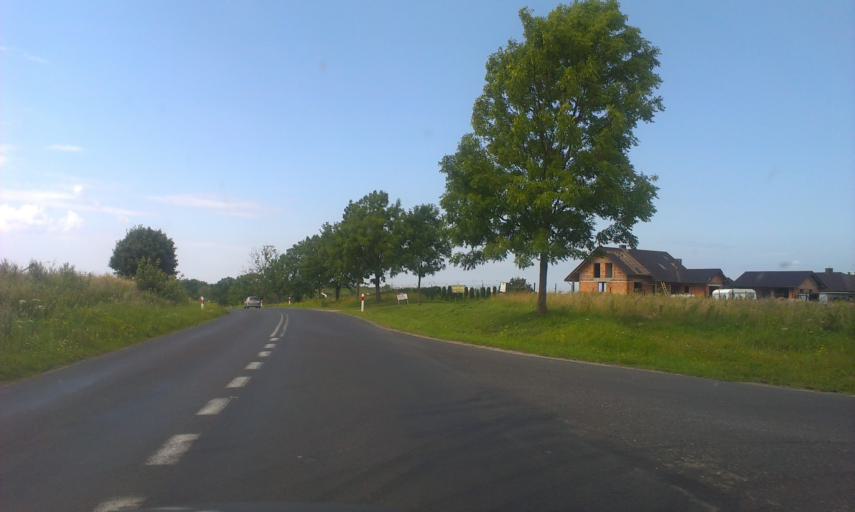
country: PL
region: West Pomeranian Voivodeship
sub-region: Powiat kolobrzeski
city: Kolobrzeg
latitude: 54.1530
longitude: 15.6317
